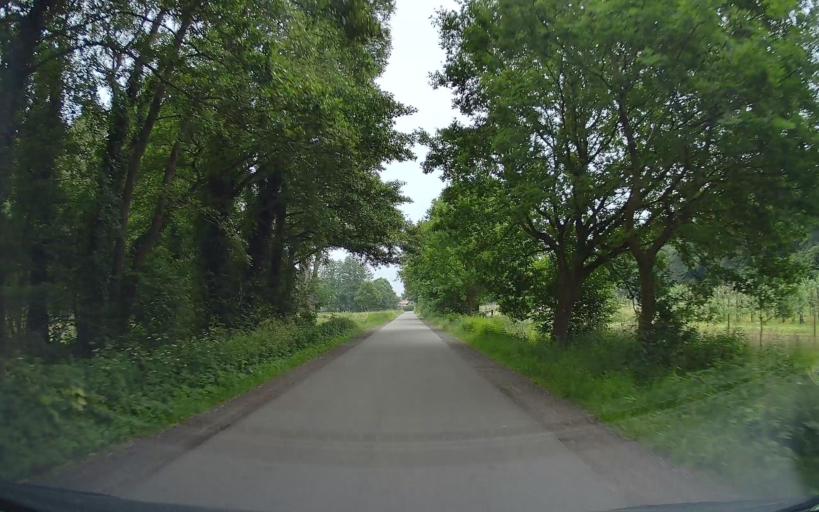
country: DE
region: Lower Saxony
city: Friesoythe
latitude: 53.0359
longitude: 7.8686
